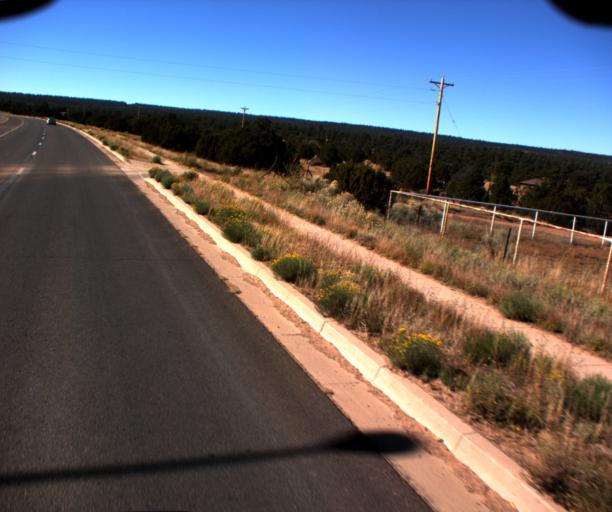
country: US
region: Arizona
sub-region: Apache County
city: Saint Michaels
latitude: 35.6592
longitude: -109.1170
